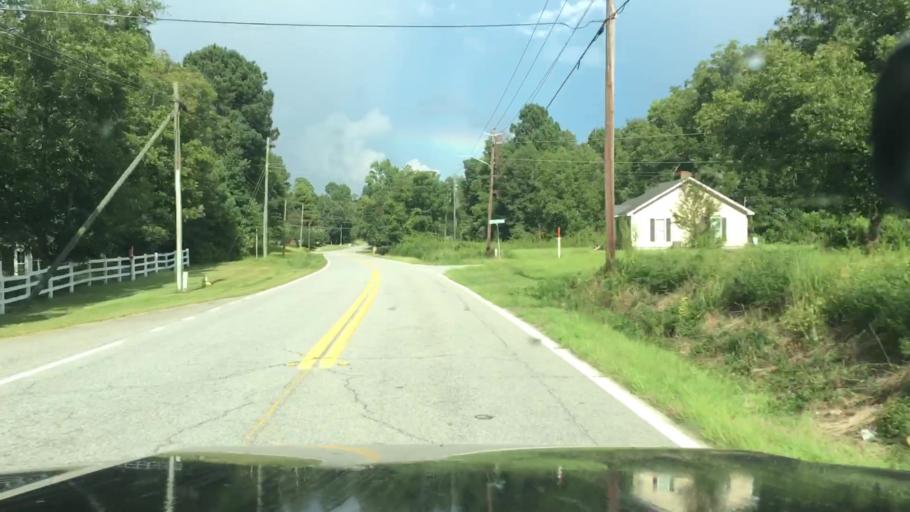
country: US
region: Georgia
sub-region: Bibb County
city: West Point
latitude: 32.8077
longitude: -83.7844
